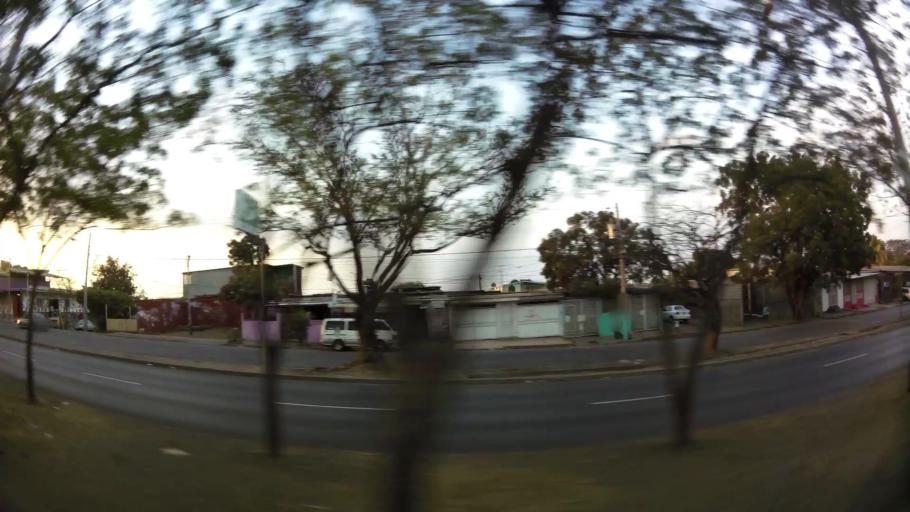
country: NI
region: Managua
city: Managua
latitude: 12.1398
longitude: -86.2121
